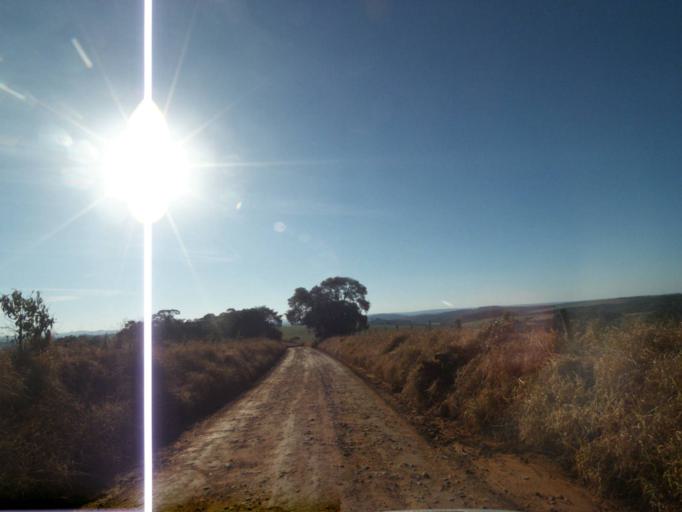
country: BR
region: Parana
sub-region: Telemaco Borba
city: Telemaco Borba
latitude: -24.5346
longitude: -50.6280
